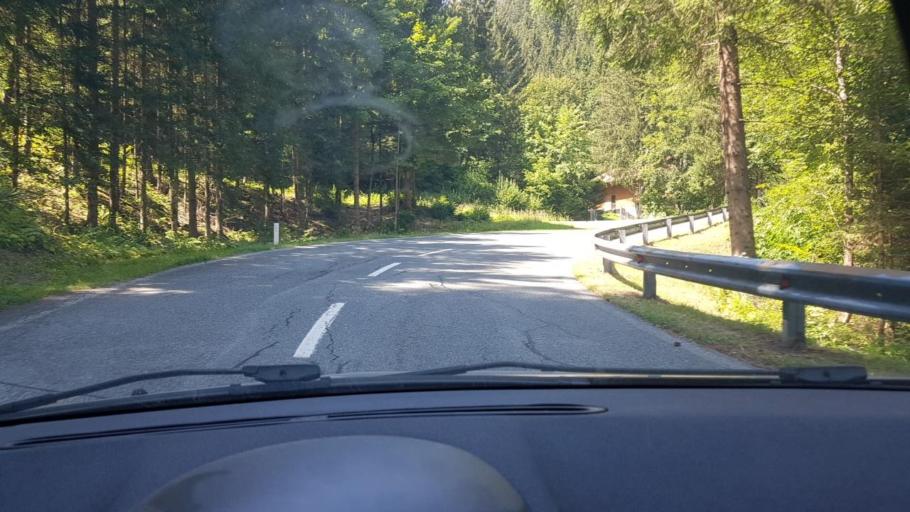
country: SI
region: Jezersko
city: Zgornje Jezersko
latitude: 46.4229
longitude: 14.5454
